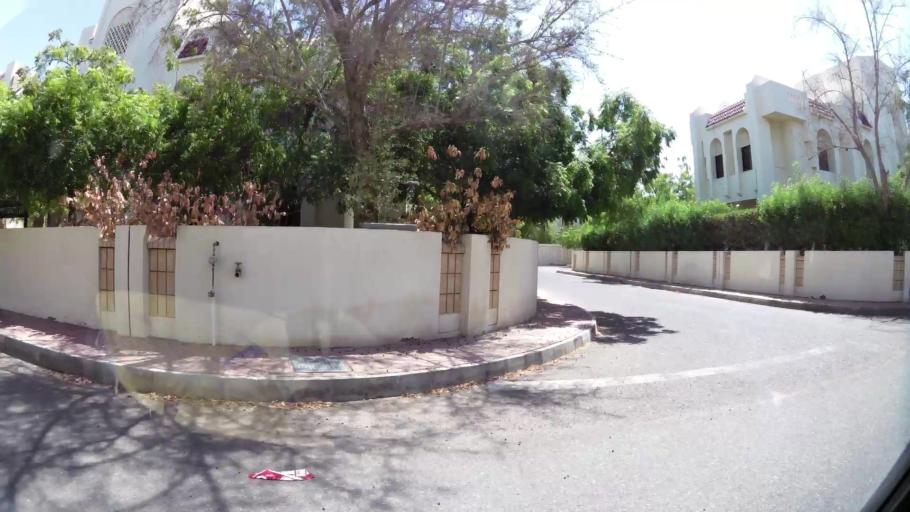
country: OM
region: Muhafazat Masqat
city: As Sib al Jadidah
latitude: 23.6149
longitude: 58.2456
